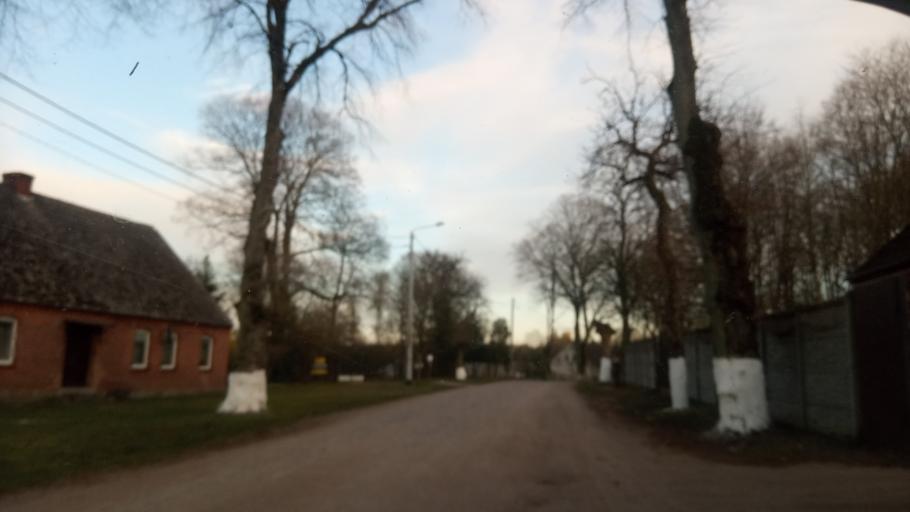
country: PL
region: West Pomeranian Voivodeship
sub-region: Powiat szczecinecki
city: Lubowo
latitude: 53.5507
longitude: 16.3948
